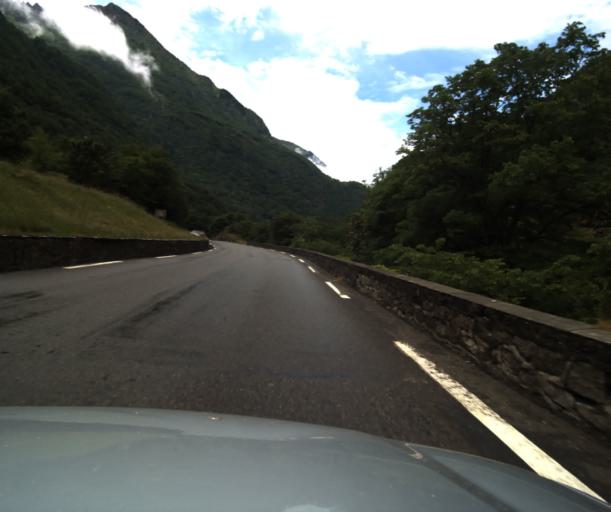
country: FR
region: Midi-Pyrenees
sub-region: Departement des Hautes-Pyrenees
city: Luz-Saint-Sauveur
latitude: 42.8354
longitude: -0.0011
